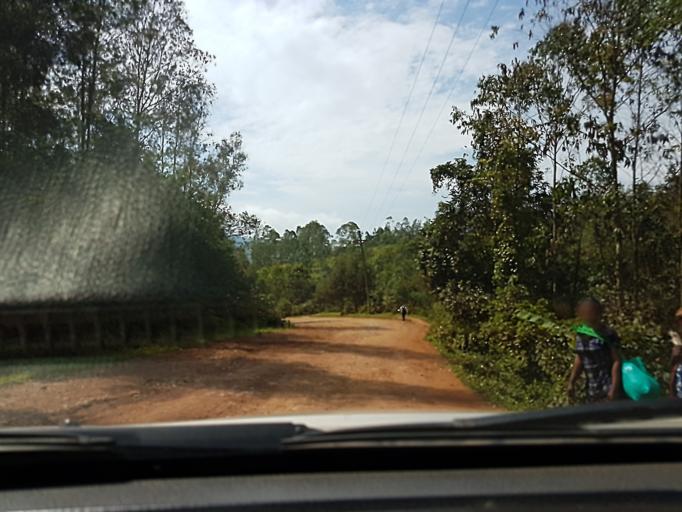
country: CD
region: South Kivu
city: Bukavu
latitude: -2.6521
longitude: 28.8729
